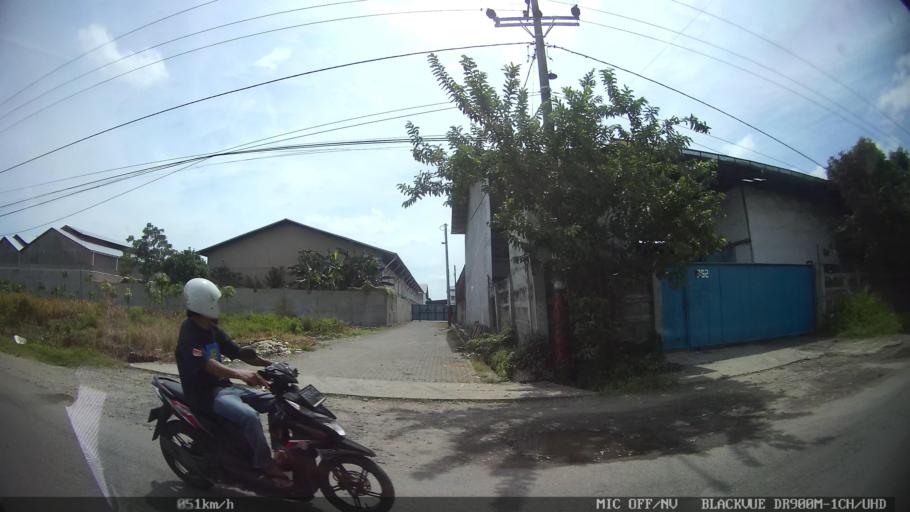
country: ID
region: North Sumatra
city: Medan
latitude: 3.6445
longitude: 98.7168
